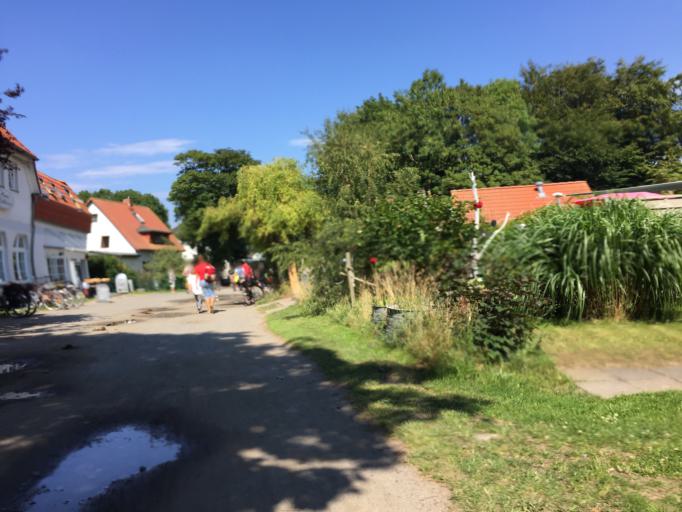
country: DE
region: Mecklenburg-Vorpommern
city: Hiddensee
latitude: 54.5862
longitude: 13.1074
